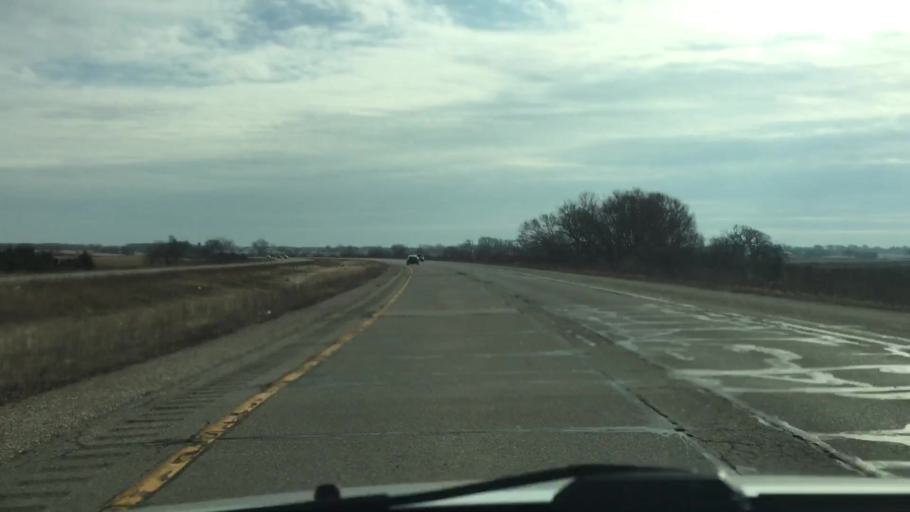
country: US
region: Wisconsin
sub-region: Walworth County
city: Como
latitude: 42.6472
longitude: -88.5035
